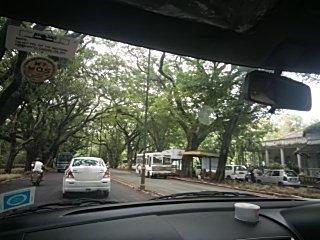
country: IN
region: Goa
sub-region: North Goa
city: Panaji
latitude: 15.4943
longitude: 73.8184
